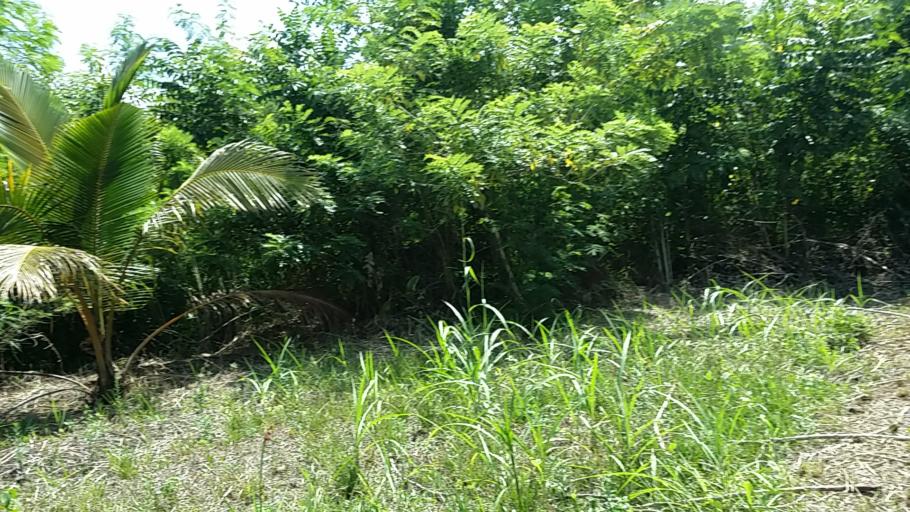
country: PH
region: Davao
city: Lacson
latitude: 7.2117
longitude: 125.4324
